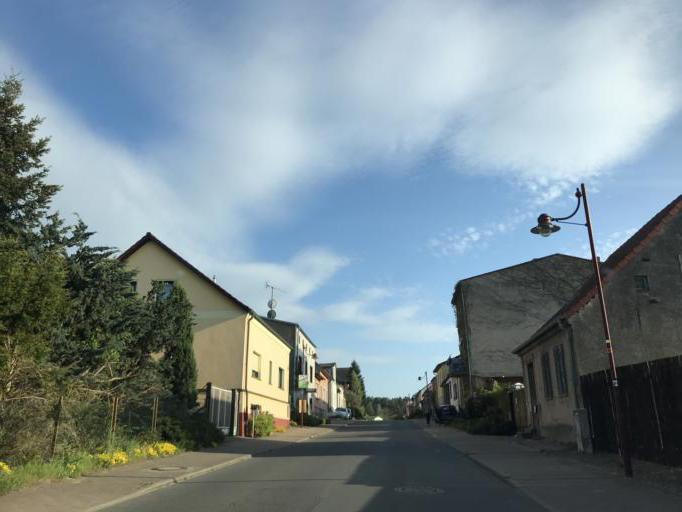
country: DE
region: Brandenburg
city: Joachimsthal
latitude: 52.9754
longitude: 13.7415
